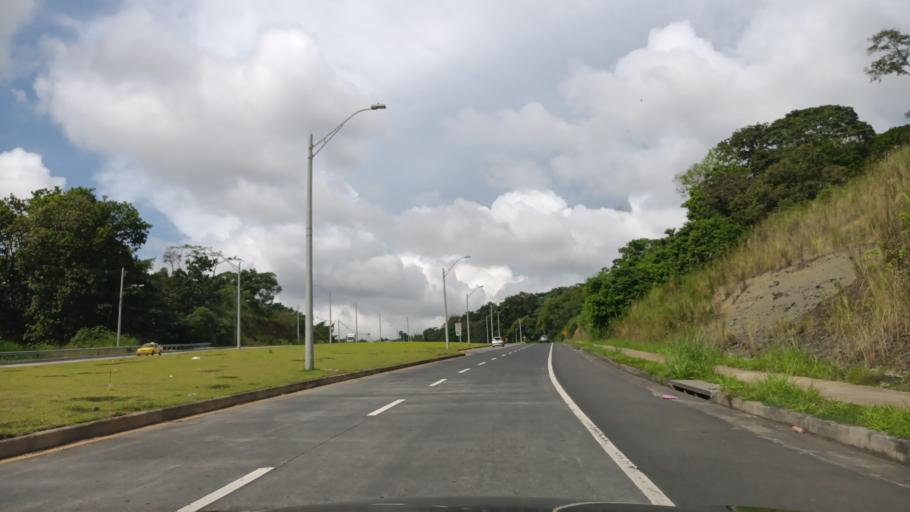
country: PA
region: Panama
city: Las Cumbres
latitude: 9.1033
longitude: -79.5244
